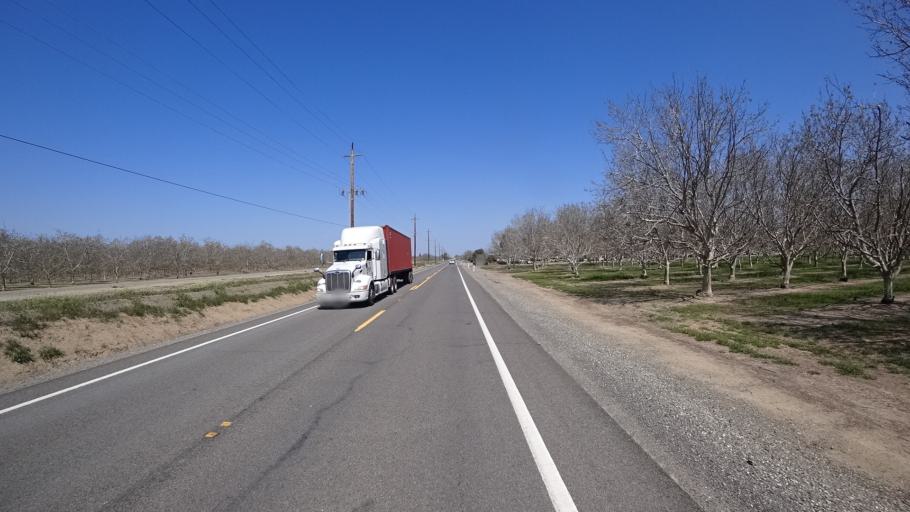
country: US
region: California
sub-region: Glenn County
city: Willows
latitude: 39.5025
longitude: -122.0187
